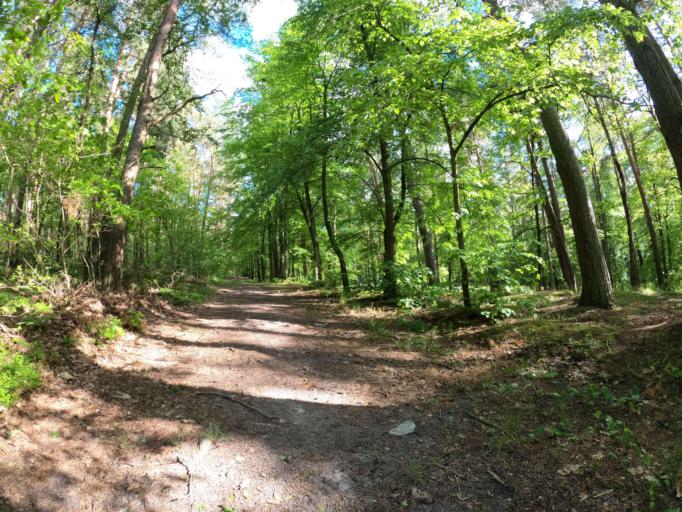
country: PL
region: Warmian-Masurian Voivodeship
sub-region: Powiat lidzbarski
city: Lidzbark Warminski
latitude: 54.1279
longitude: 20.6094
